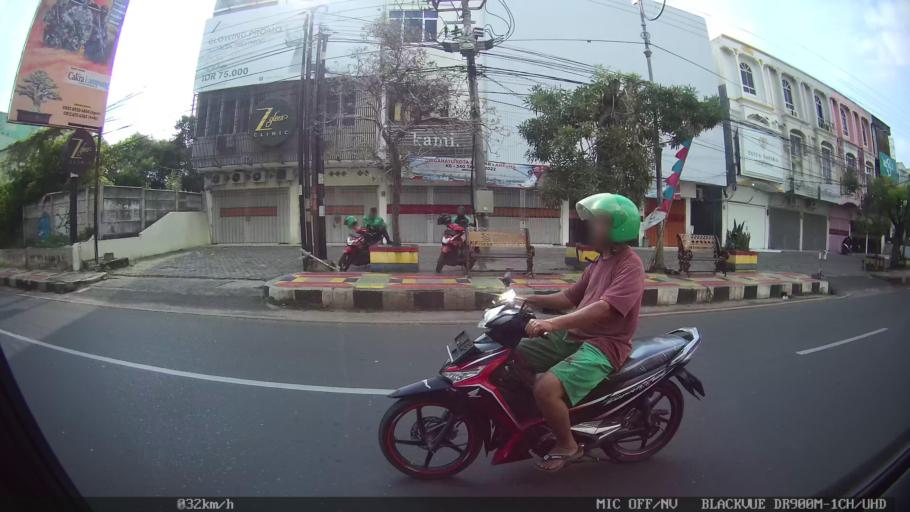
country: ID
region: Lampung
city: Bandarlampung
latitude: -5.4205
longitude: 105.2524
